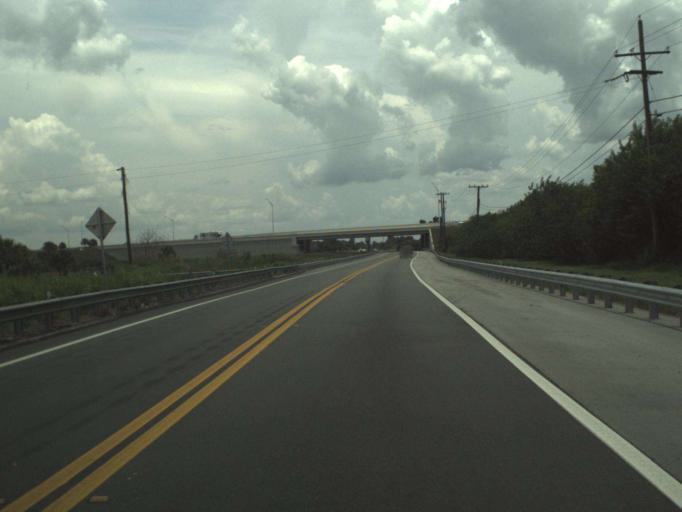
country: US
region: Florida
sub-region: Saint Lucie County
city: Lakewood Park
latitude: 27.4519
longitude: -80.3990
